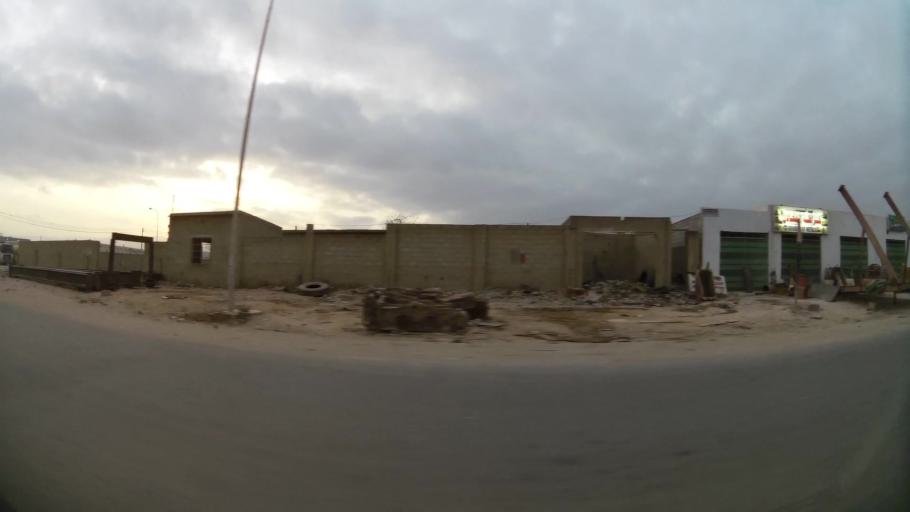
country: OM
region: Zufar
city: Salalah
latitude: 17.0256
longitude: 54.0409
